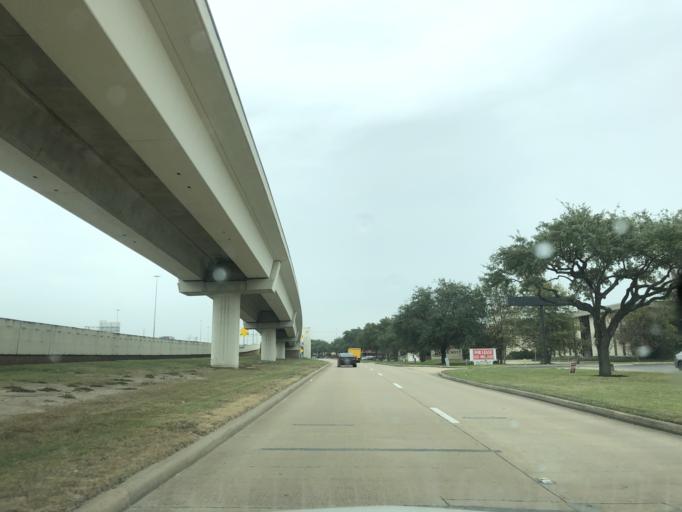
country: US
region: Texas
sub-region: Fort Bend County
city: Meadows Place
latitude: 29.6235
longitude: -95.5981
